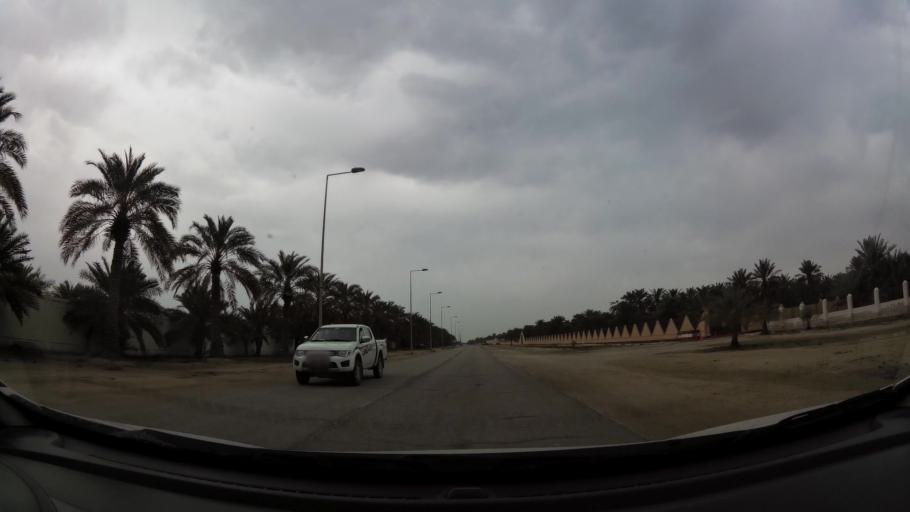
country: BH
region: Central Governorate
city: Dar Kulayb
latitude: 26.0388
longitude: 50.4874
